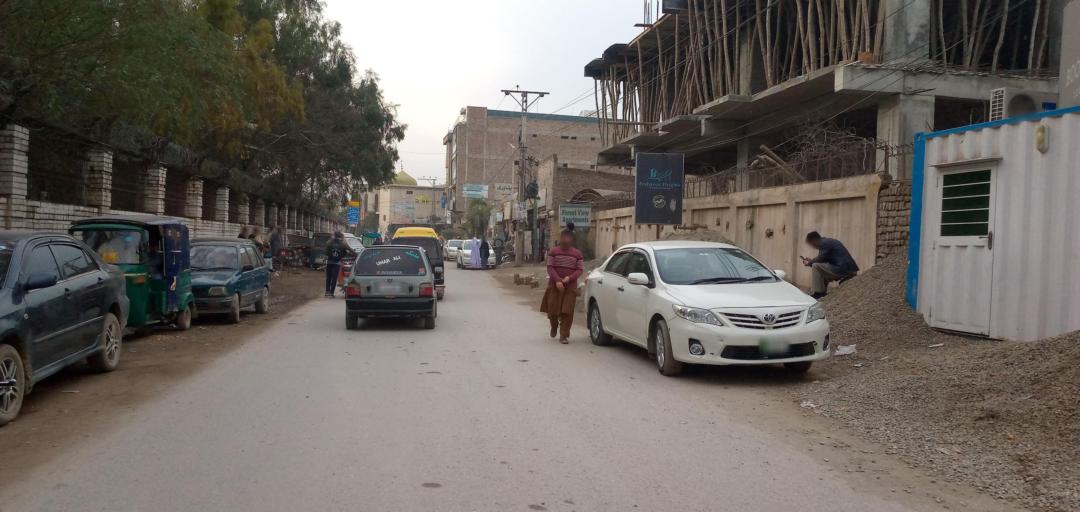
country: PK
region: Khyber Pakhtunkhwa
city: Peshawar
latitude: 34.0232
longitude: 71.4871
